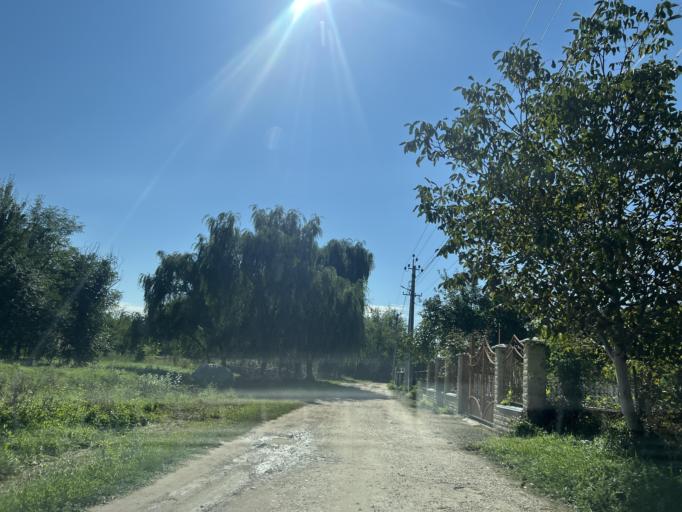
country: RO
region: Iasi
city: Ungheni-Prut
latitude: 47.1985
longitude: 27.7900
